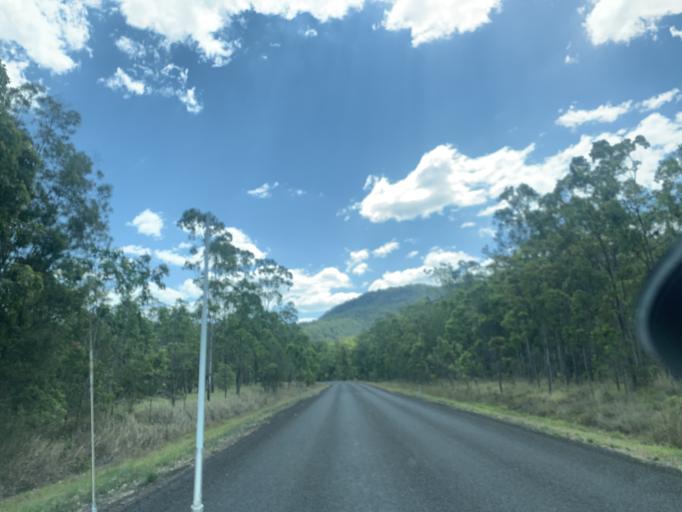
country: AU
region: Queensland
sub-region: Tablelands
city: Atherton
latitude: -17.3197
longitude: 145.4447
